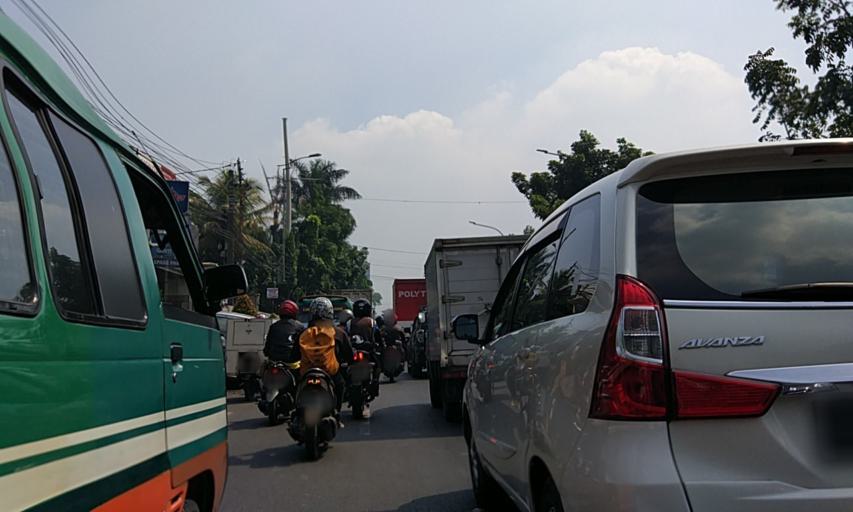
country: ID
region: West Java
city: Cimahi
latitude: -6.9076
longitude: 107.5673
